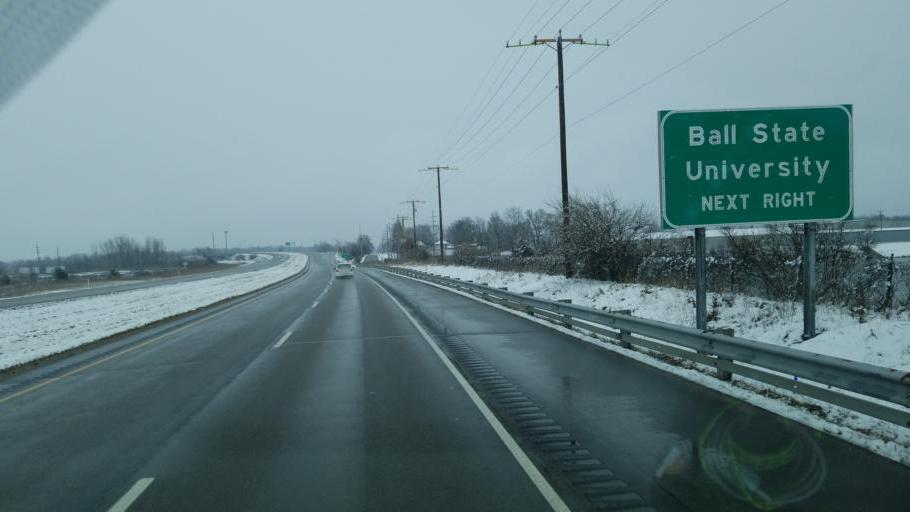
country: US
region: Indiana
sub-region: Delaware County
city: Muncie
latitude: 40.2519
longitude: -85.3679
